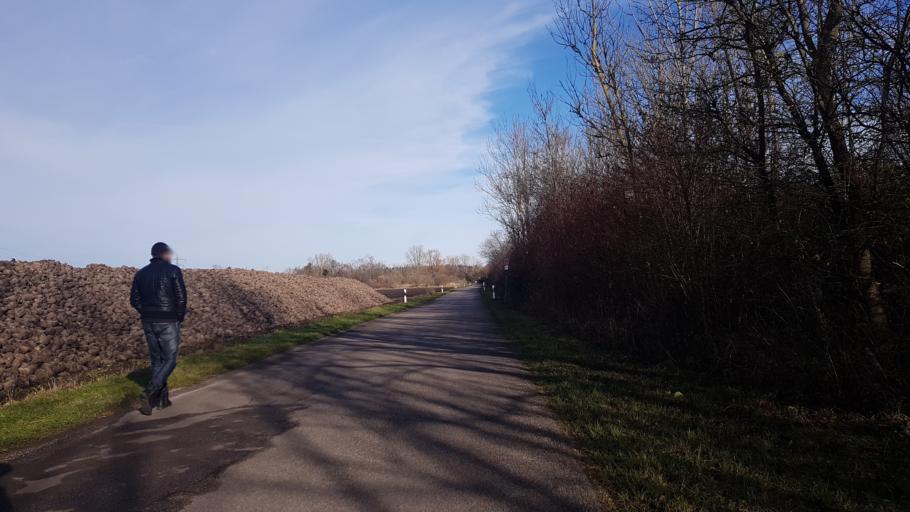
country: DE
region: Bavaria
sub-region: Upper Bavaria
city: Karlsfeld
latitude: 48.2400
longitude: 11.5089
